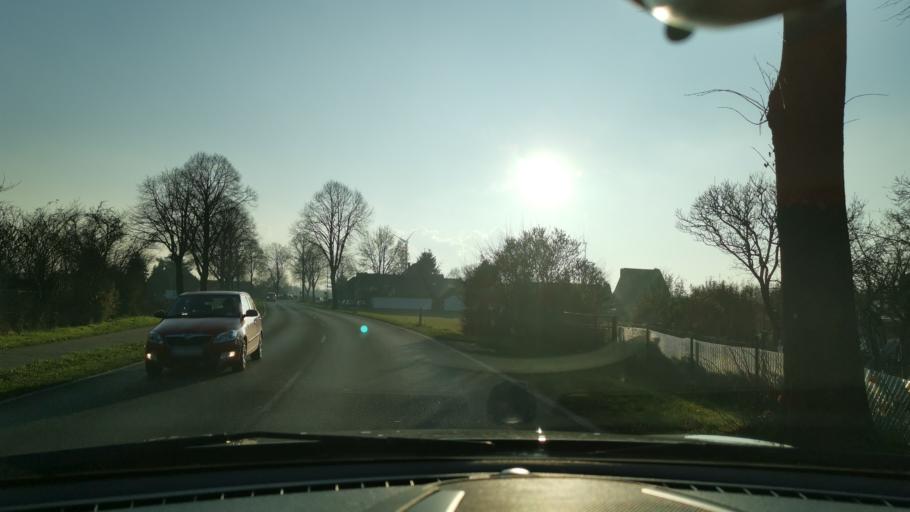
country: DE
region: North Rhine-Westphalia
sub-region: Regierungsbezirk Dusseldorf
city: Neuss
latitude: 51.1450
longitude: 6.7127
